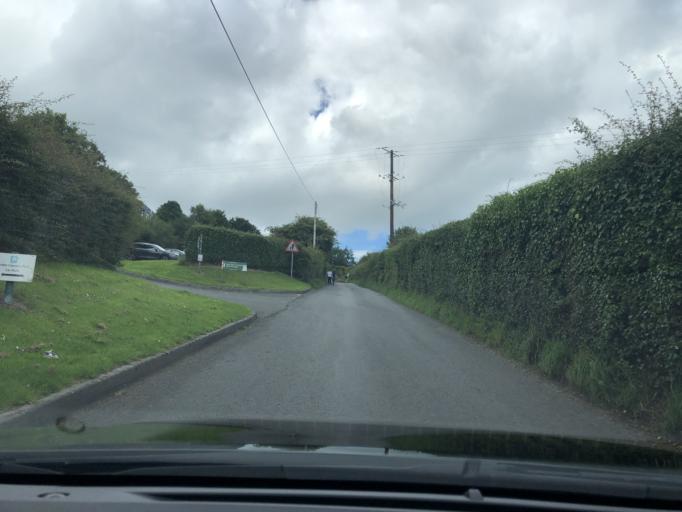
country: GB
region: Northern Ireland
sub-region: Ards District
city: Newtownards
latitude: 54.5769
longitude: -5.7177
